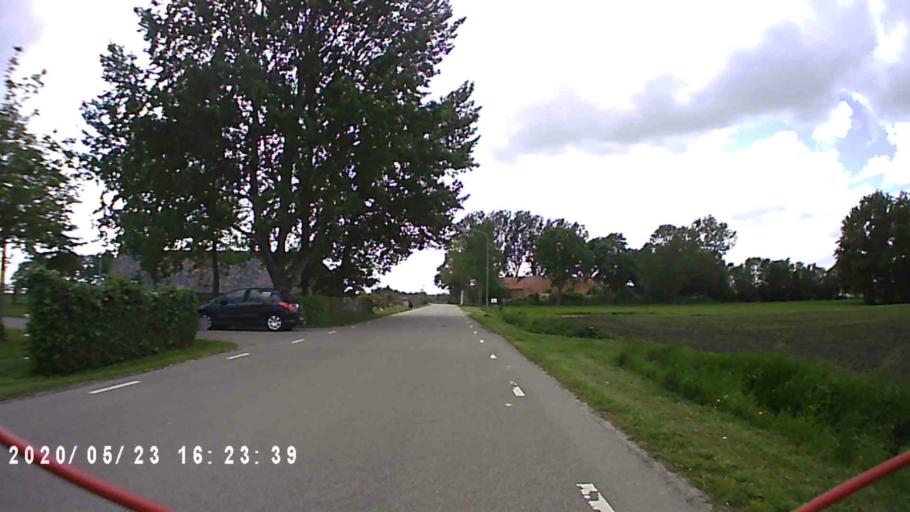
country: NL
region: Groningen
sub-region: Gemeente Appingedam
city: Appingedam
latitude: 53.2661
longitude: 6.8590
